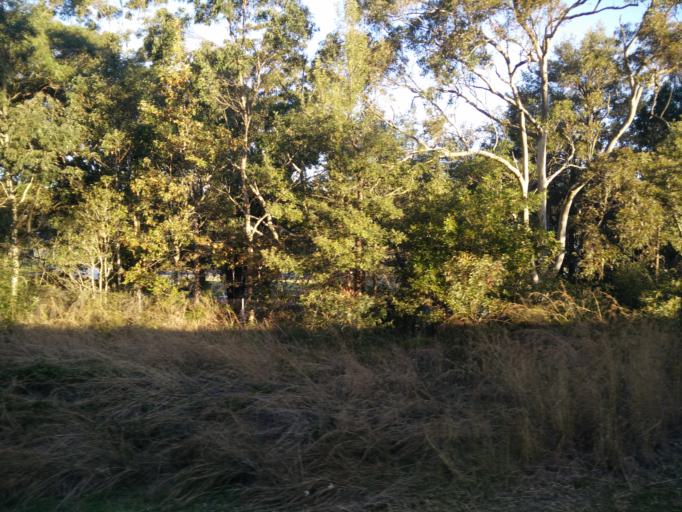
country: AU
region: New South Wales
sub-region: Lake Macquarie Shire
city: Kotara
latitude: -32.9416
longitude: 151.6985
